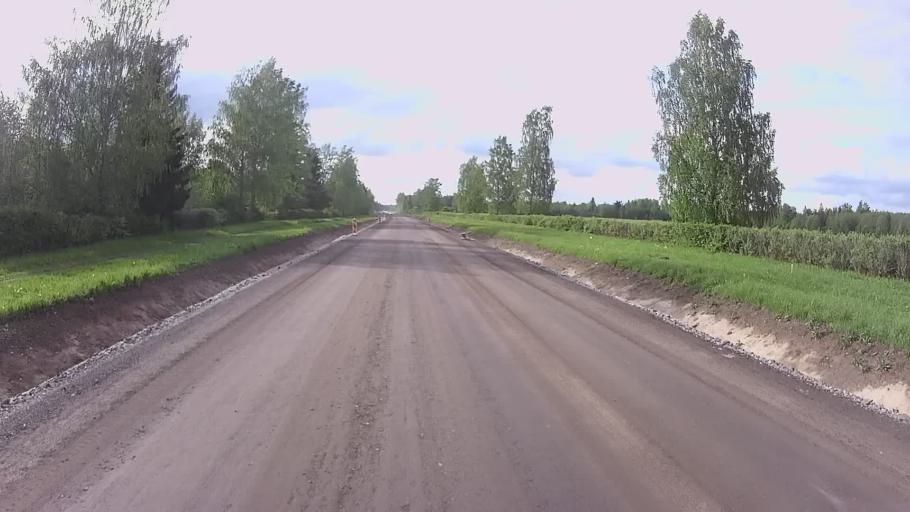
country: EE
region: Jogevamaa
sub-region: Mustvee linn
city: Mustvee
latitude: 59.0225
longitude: 26.6998
